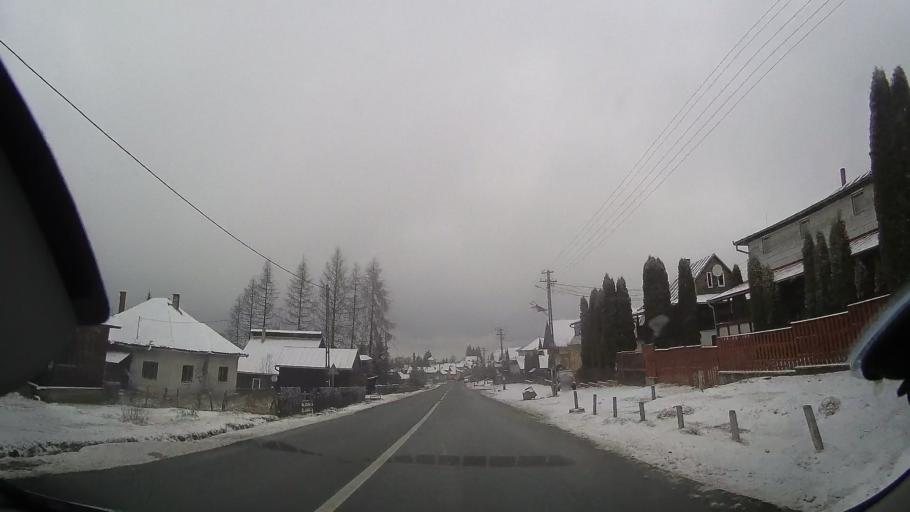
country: RO
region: Cluj
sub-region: Comuna Belis
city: Belis
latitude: 46.6823
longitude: 23.0334
